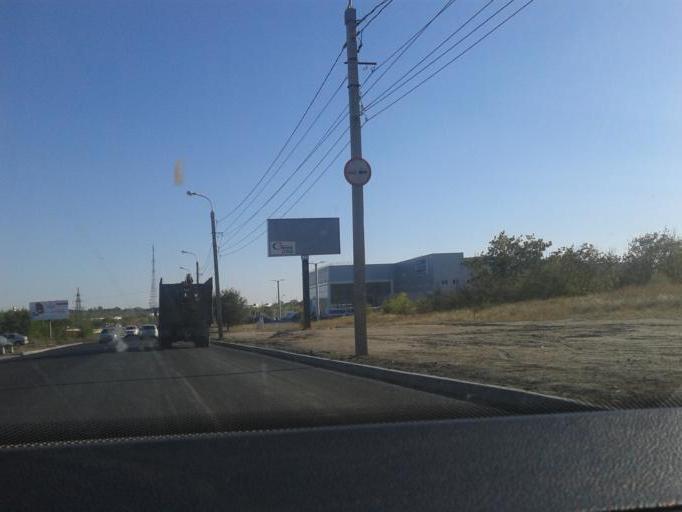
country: RU
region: Volgograd
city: Volgograd
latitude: 48.7581
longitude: 44.5229
